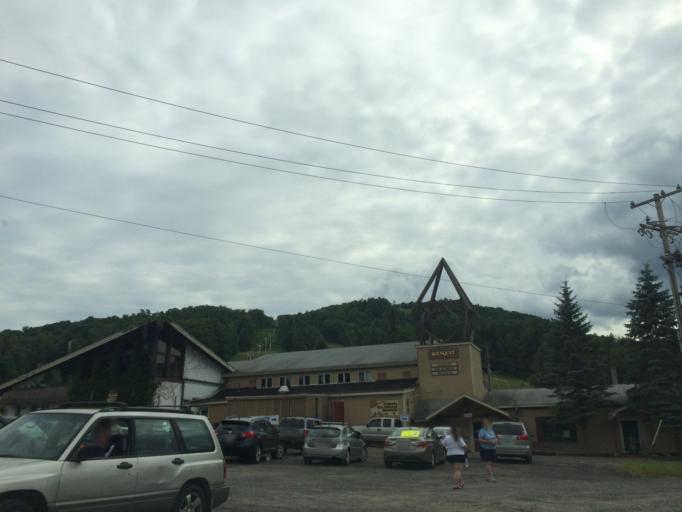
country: US
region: Massachusetts
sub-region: Berkshire County
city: Pittsfield
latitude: 42.4195
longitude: -73.2767
